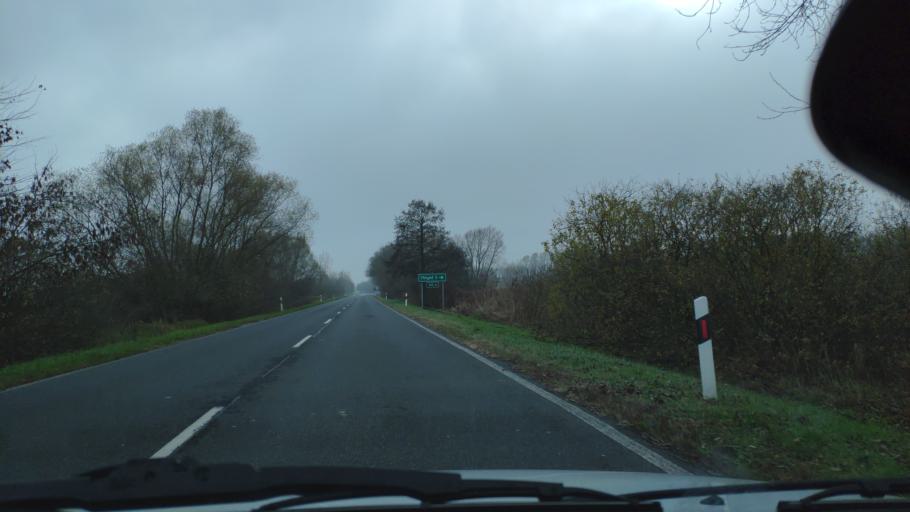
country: HU
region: Somogy
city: Balatonbereny
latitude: 46.6070
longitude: 17.2708
